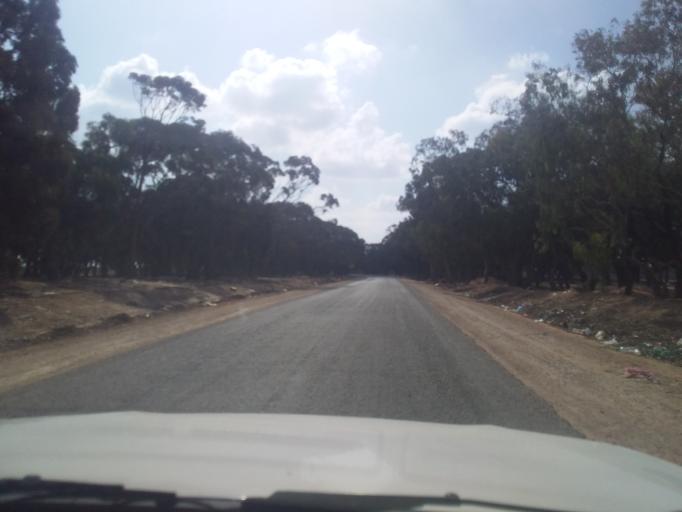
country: TN
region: Qabis
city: Gabes
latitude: 33.6281
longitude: 10.2707
